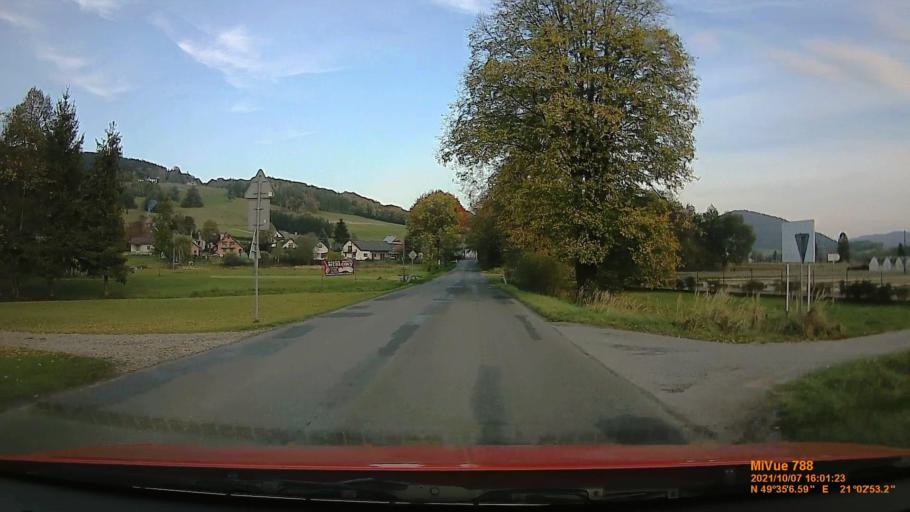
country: PL
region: Lesser Poland Voivodeship
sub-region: Powiat gorlicki
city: Ropa
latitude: 49.5851
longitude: 21.0481
